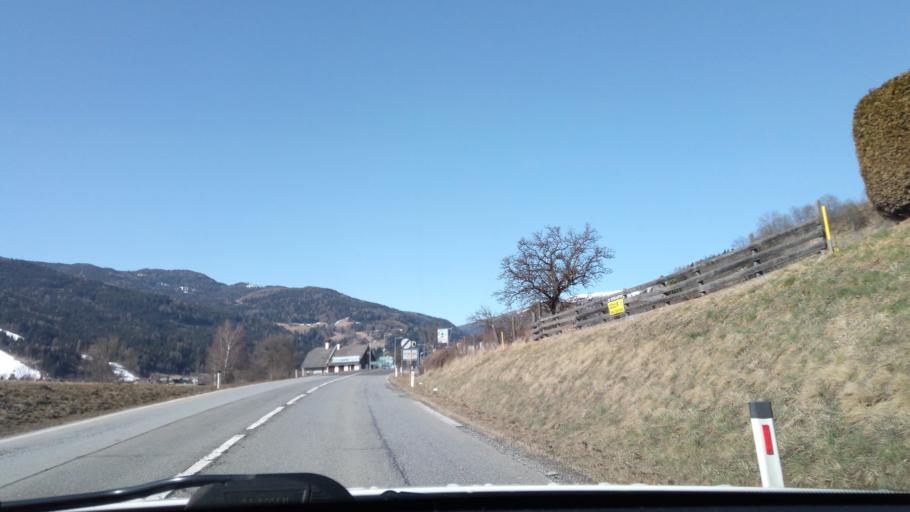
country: AT
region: Styria
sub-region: Politischer Bezirk Murau
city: Sankt Georgen ob Murau
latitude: 47.1043
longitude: 14.1017
